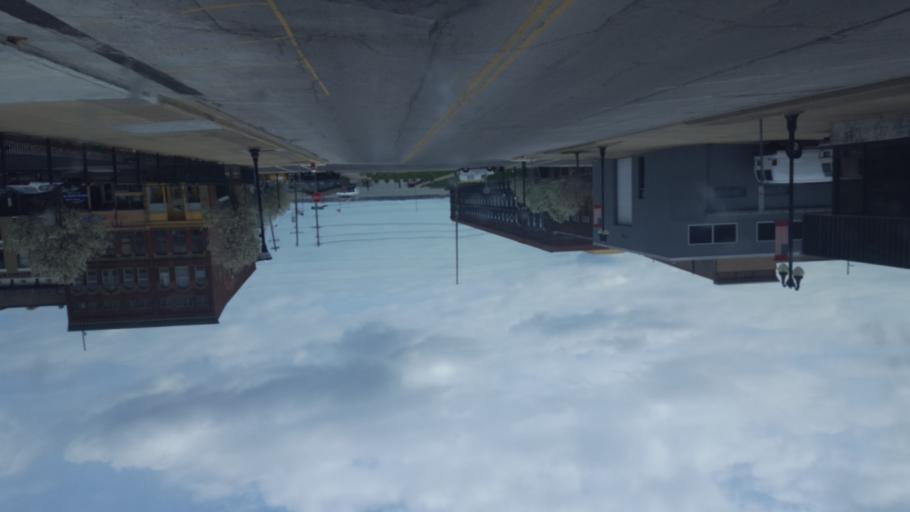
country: US
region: Ohio
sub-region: Erie County
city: Sandusky
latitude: 41.4562
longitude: -82.7136
